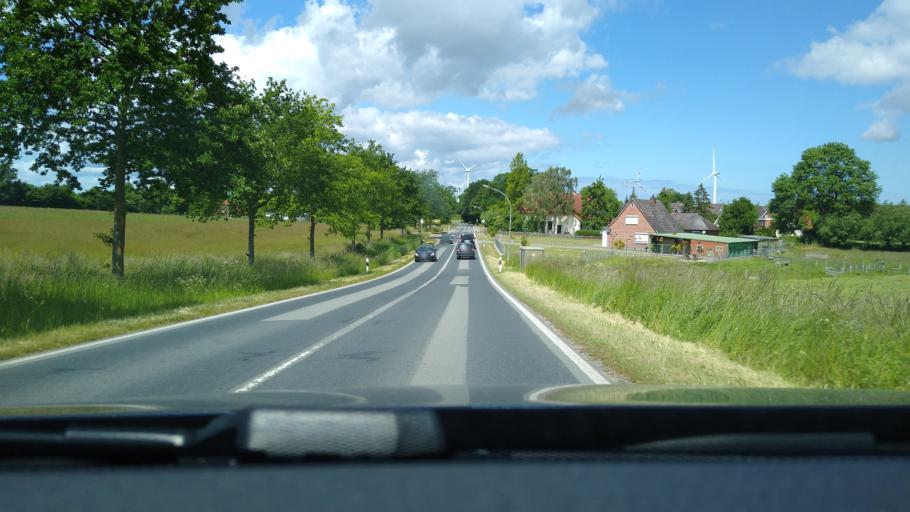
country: DE
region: Schleswig-Holstein
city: Kabelhorst
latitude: 54.2140
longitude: 10.9247
